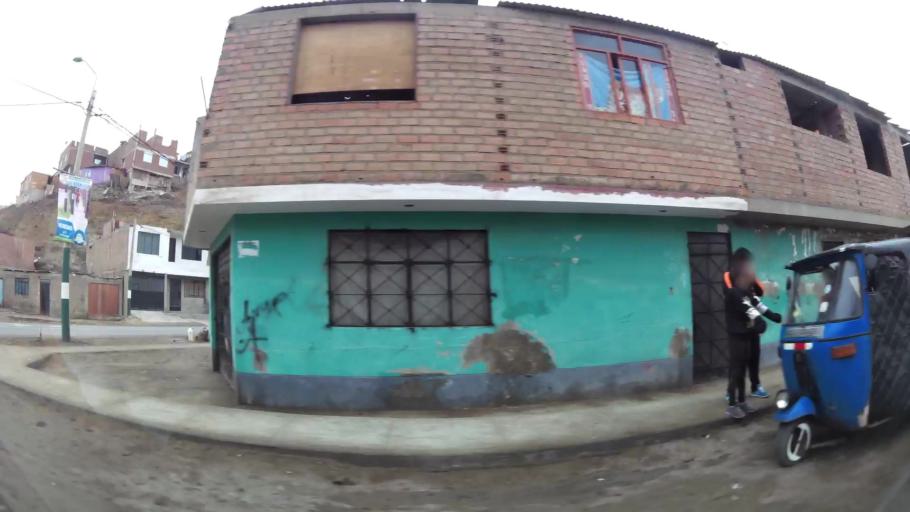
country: PE
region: Lima
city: Ventanilla
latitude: -11.8789
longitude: -77.1337
